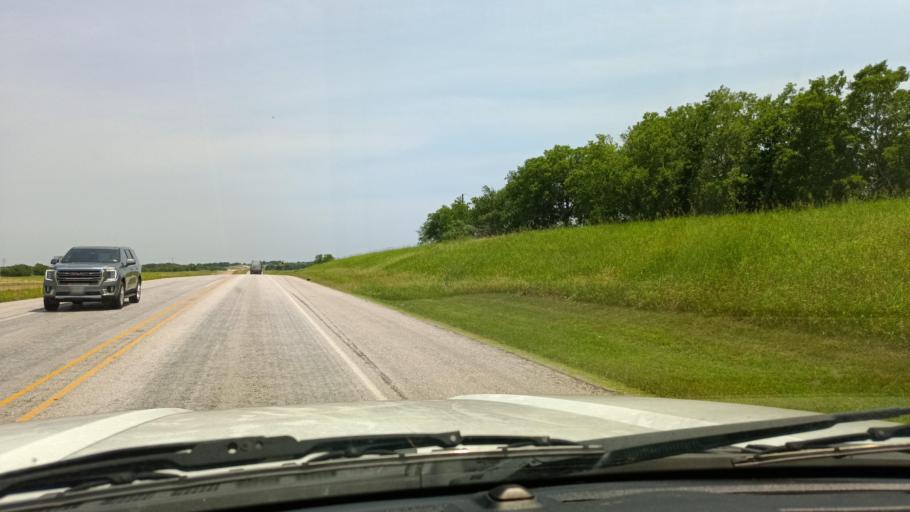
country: US
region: Texas
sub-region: Bell County
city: Rogers
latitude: 30.9698
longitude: -97.2674
